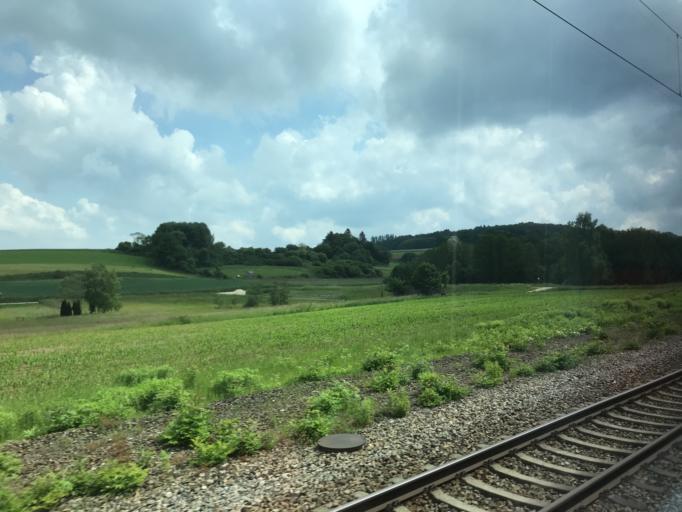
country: DE
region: Bavaria
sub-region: Swabia
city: Jettingen-Scheppach
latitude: 48.3978
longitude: 10.4487
